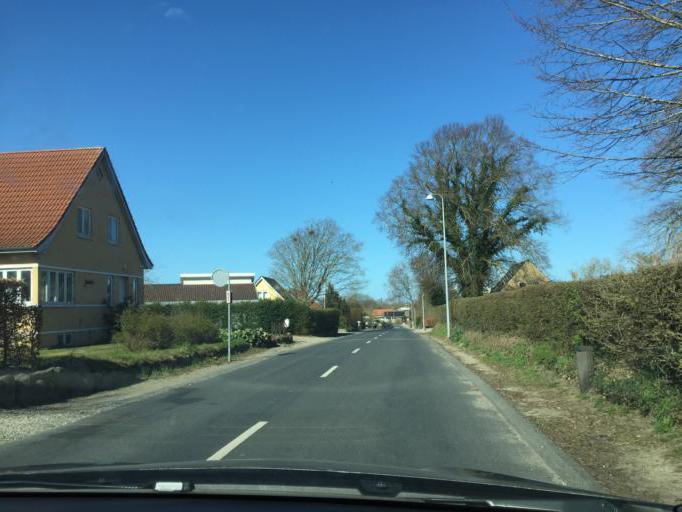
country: DK
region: South Denmark
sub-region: Kerteminde Kommune
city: Langeskov
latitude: 55.3343
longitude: 10.5432
